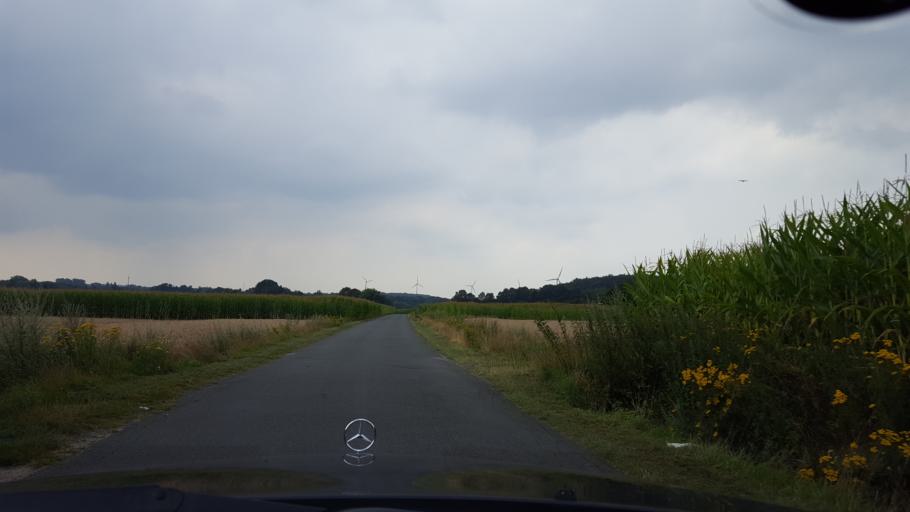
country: DE
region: North Rhine-Westphalia
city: Oer-Erkenschwick
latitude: 51.6547
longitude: 7.2333
